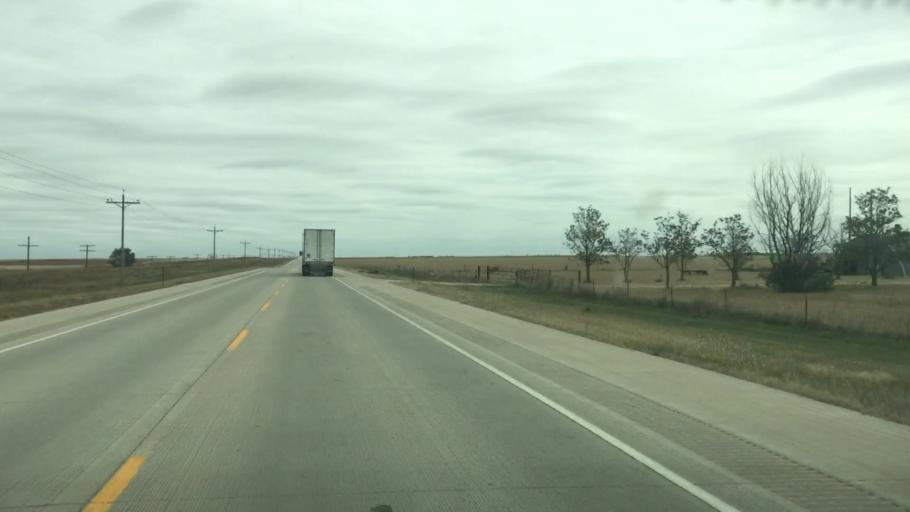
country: US
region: Colorado
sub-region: Kiowa County
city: Eads
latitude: 38.4750
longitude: -102.7518
